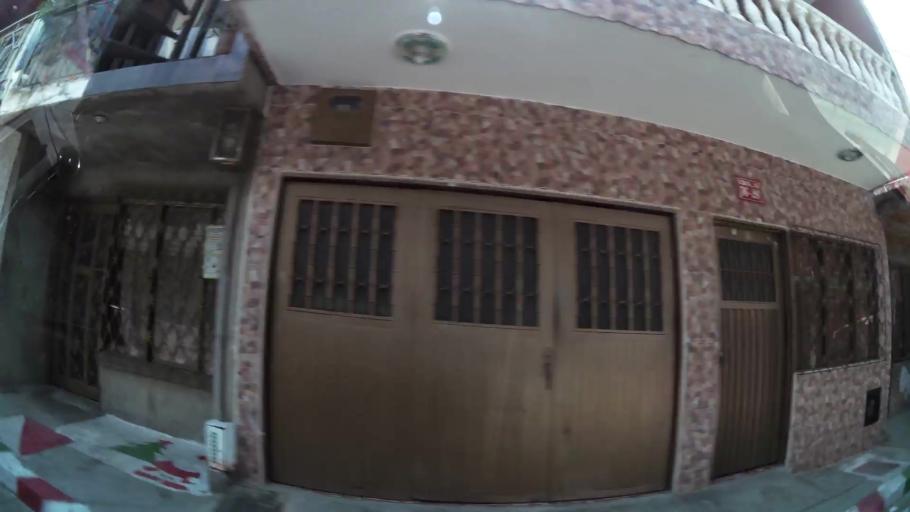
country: CO
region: Valle del Cauca
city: Cali
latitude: 3.4758
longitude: -76.4809
